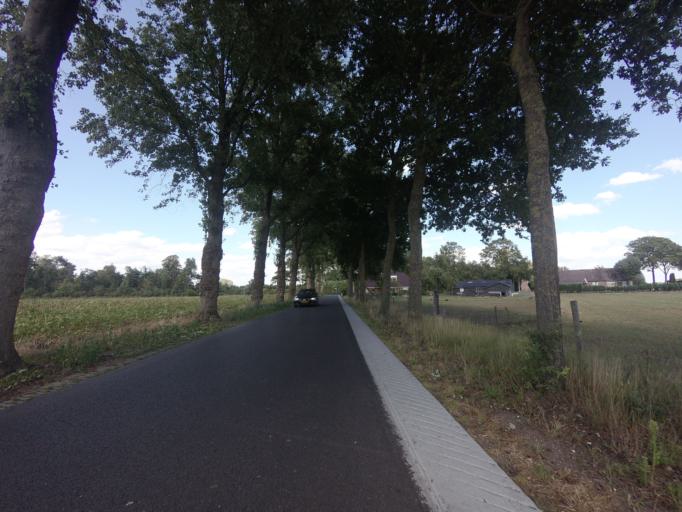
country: NL
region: Drenthe
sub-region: Gemeente Hoogeveen
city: Hoogeveen
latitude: 52.6155
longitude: 6.4742
